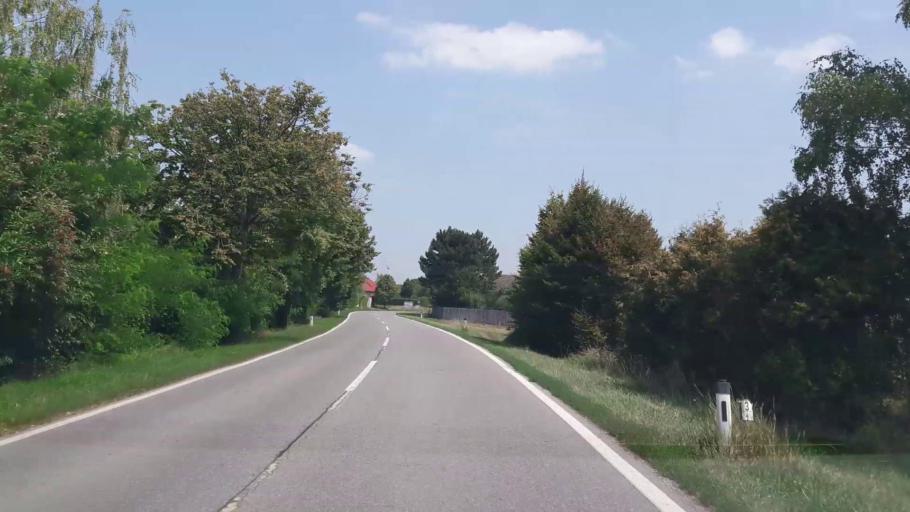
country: AT
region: Lower Austria
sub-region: Politischer Bezirk Bruck an der Leitha
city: Trautmannsdorf an der Leitha
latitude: 48.0214
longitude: 16.6284
